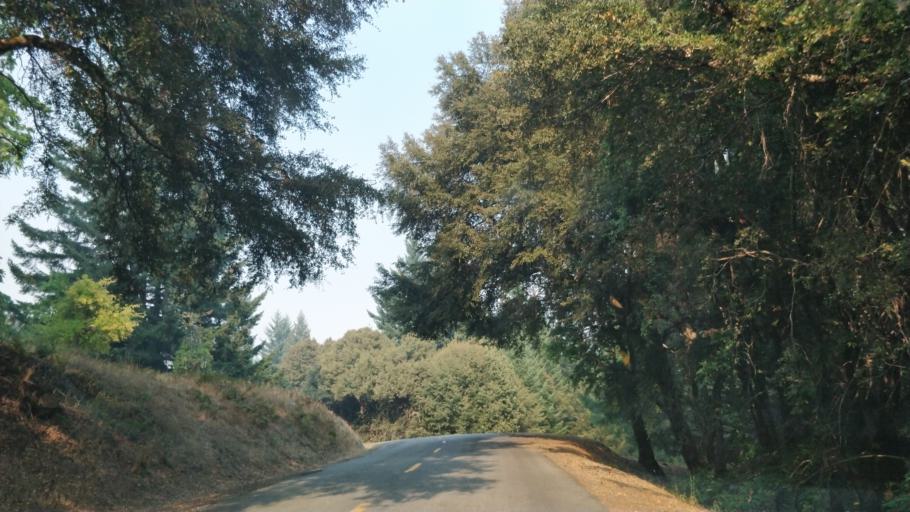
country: US
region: California
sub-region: Humboldt County
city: Rio Dell
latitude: 40.2794
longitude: -124.0681
